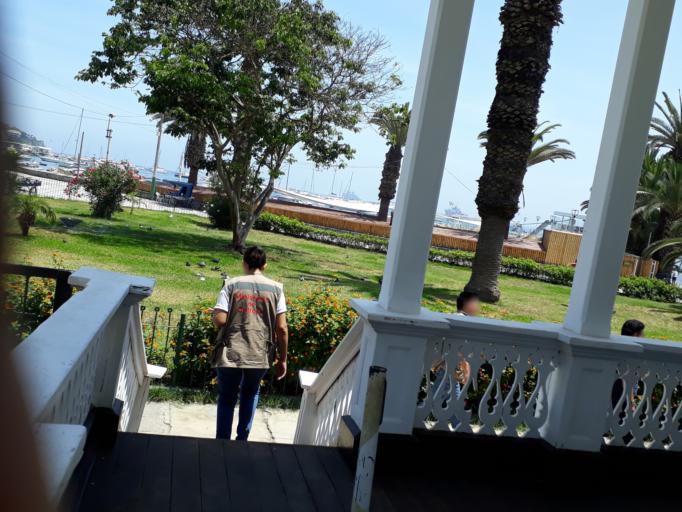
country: PE
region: Lima
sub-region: Lima
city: Santa Rosa
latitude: -11.7759
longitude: -77.1781
